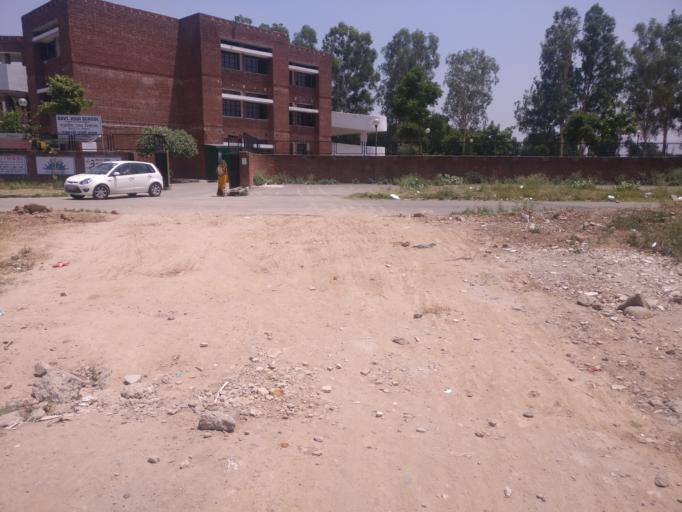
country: IN
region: Punjab
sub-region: Ajitgarh
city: Mohali
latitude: 30.7281
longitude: 76.7289
